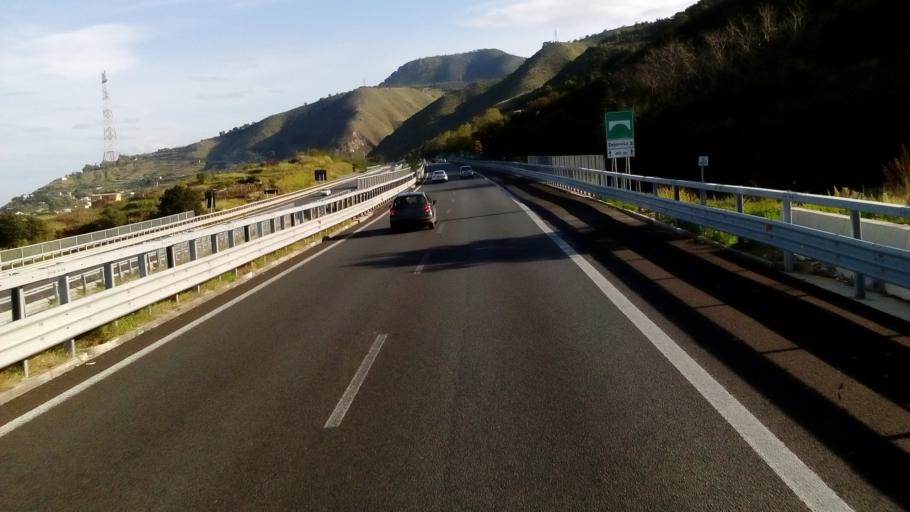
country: IT
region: Calabria
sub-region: Provincia di Reggio Calabria
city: Villa San Giovanni
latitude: 38.2312
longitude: 15.6637
